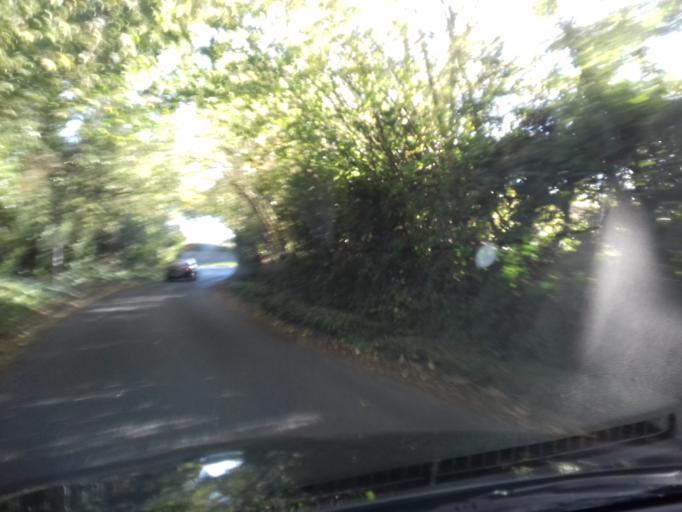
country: IE
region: Leinster
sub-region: Lu
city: Tullyallen
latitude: 53.7153
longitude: -6.3891
